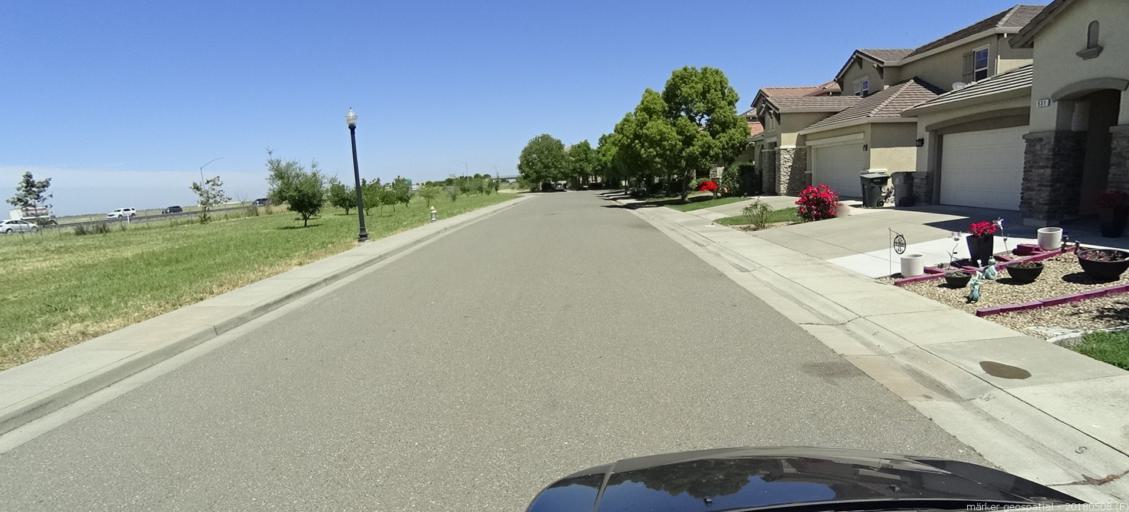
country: US
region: California
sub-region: Sacramento County
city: Elverta
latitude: 38.6796
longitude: -121.5393
